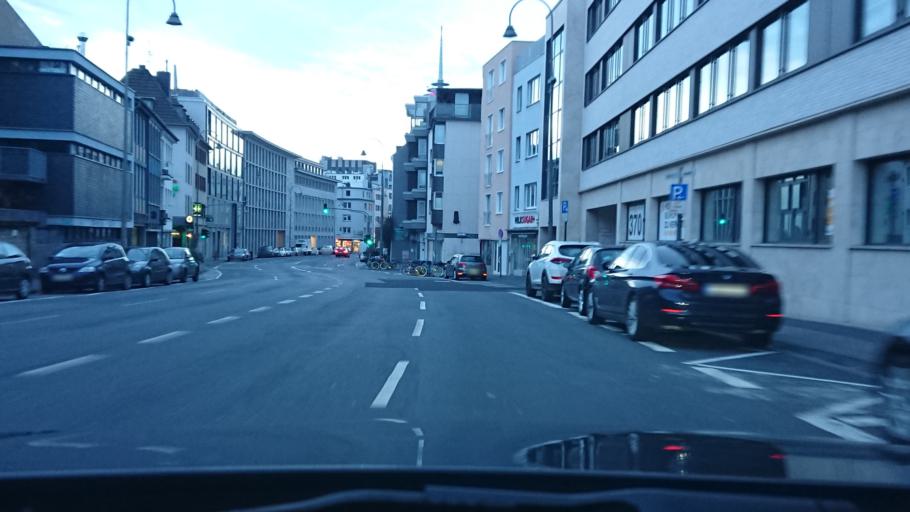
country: DE
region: North Rhine-Westphalia
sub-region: Regierungsbezirk Koln
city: Neustadt/Nord
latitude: 50.9436
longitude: 6.9465
